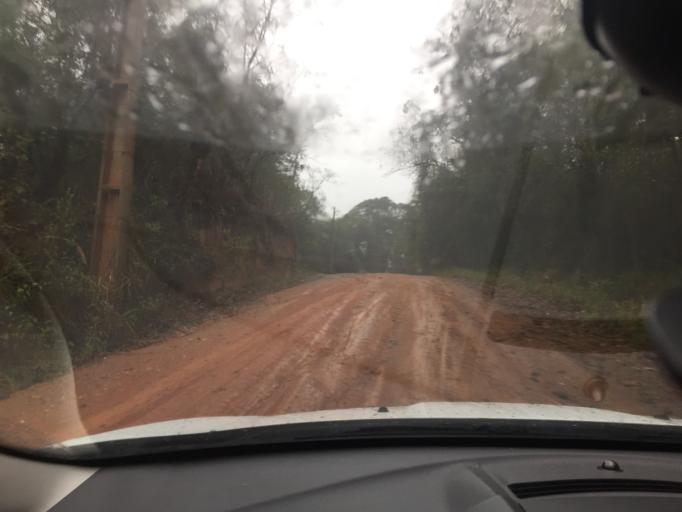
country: BR
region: Sao Paulo
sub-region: Jarinu
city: Jarinu
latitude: -23.1444
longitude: -46.7436
